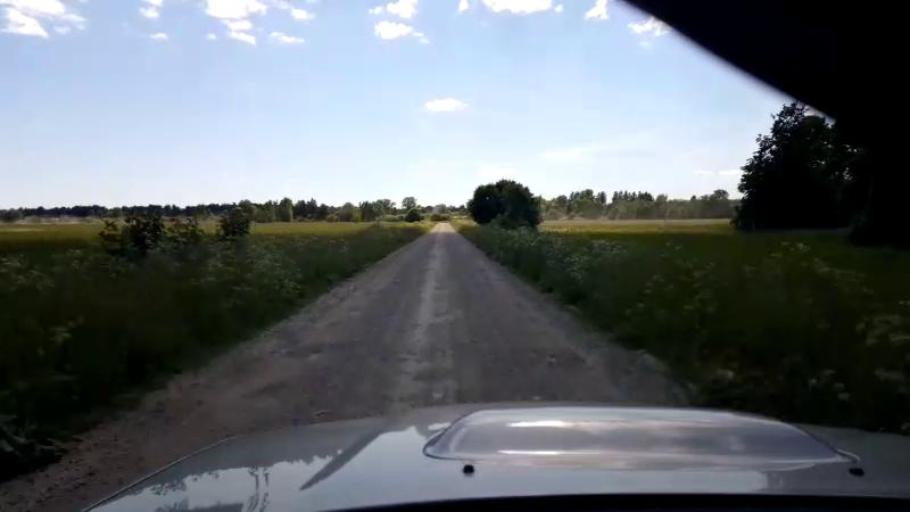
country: EE
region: Paernumaa
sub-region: Sauga vald
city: Sauga
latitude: 58.5135
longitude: 24.5113
